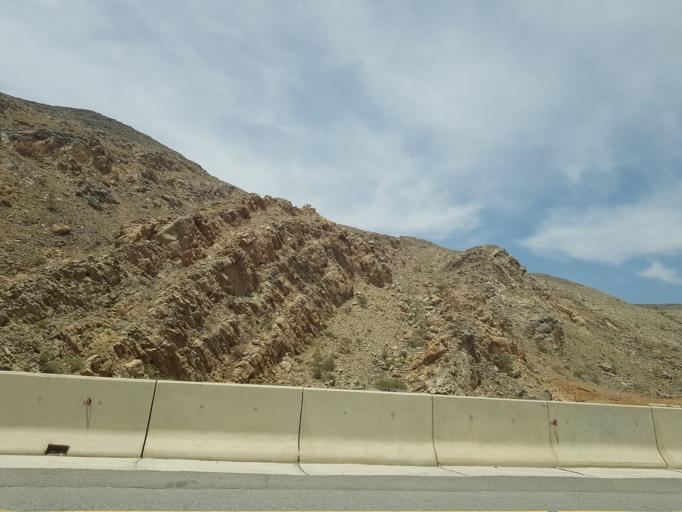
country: OM
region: Muhafazat ad Dakhiliyah
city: Izki
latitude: 22.9615
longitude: 57.6785
